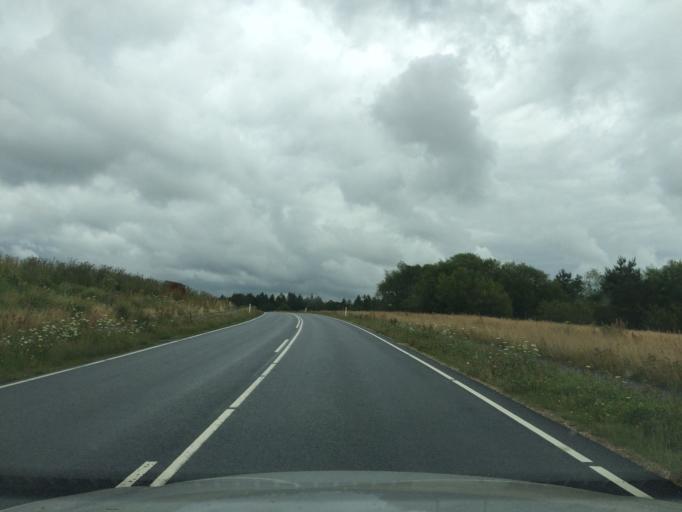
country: DK
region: Central Jutland
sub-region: Silkeborg Kommune
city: Svejbaek
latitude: 56.1860
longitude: 9.6714
